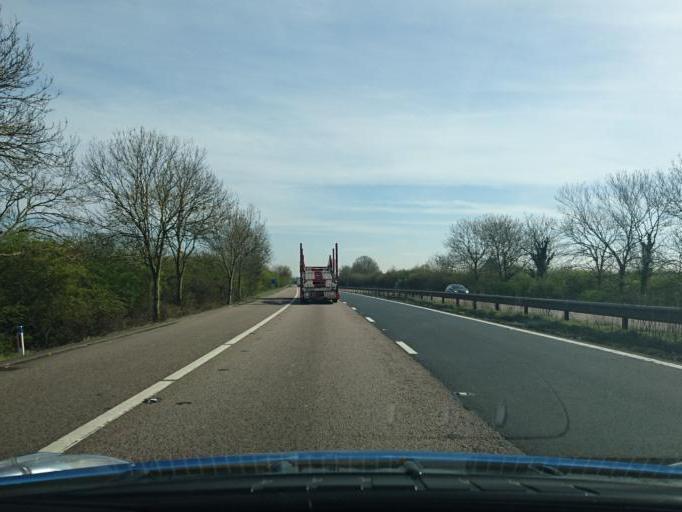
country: GB
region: England
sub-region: Worcestershire
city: Upton upon Severn
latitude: 52.0020
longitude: -2.2542
